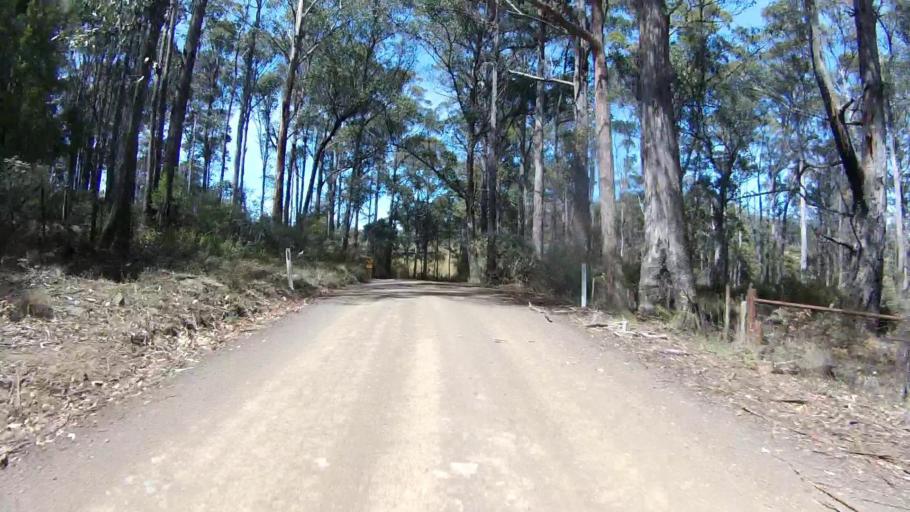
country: AU
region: Tasmania
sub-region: Sorell
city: Sorell
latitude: -42.7014
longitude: 147.7435
